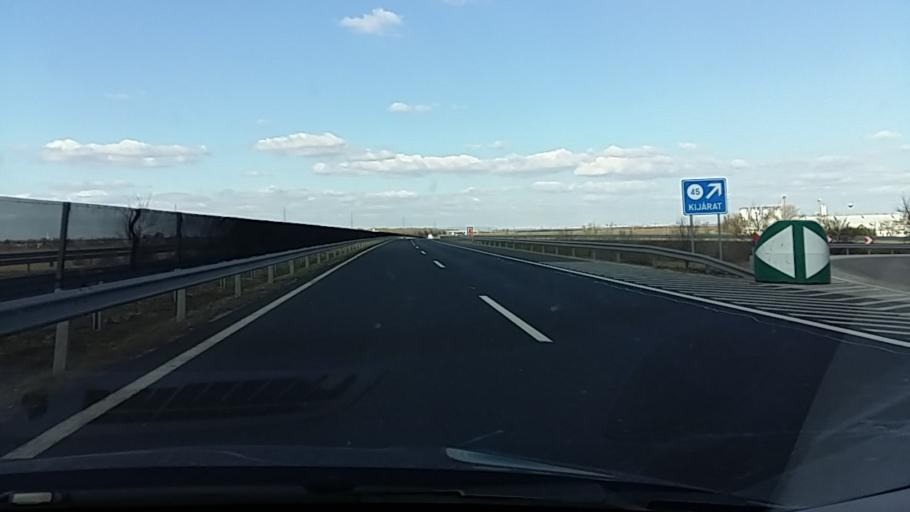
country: HU
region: Fejer
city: Ivancsa
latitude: 47.1753
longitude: 18.8055
